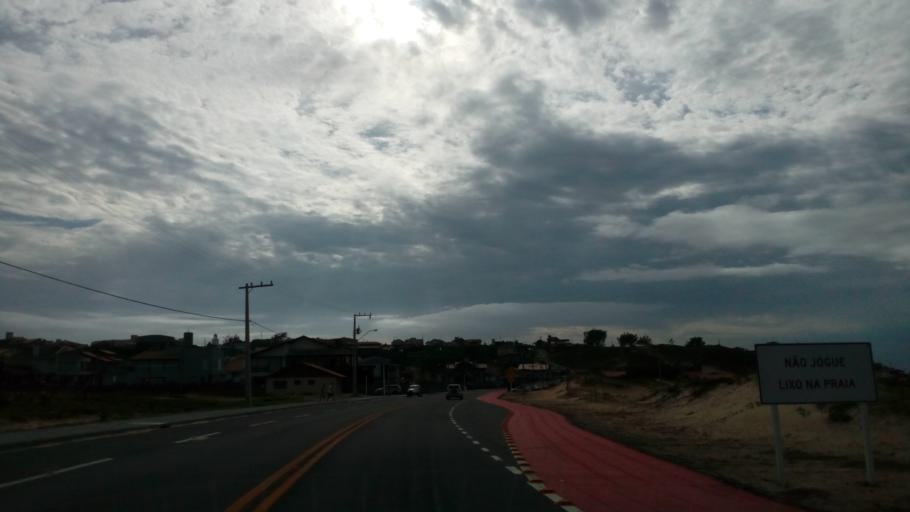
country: BR
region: Santa Catarina
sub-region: Laguna
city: Laguna
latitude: -28.6056
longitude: -48.8246
